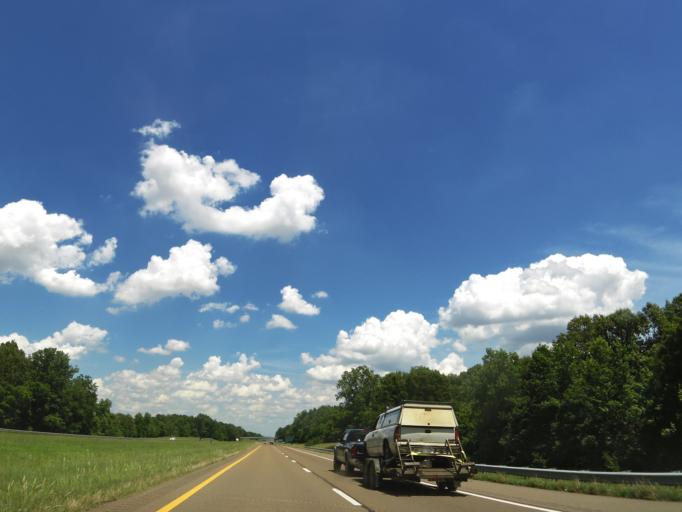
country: US
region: Tennessee
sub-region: Dyer County
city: Dyersburg
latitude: 36.0694
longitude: -89.4368
